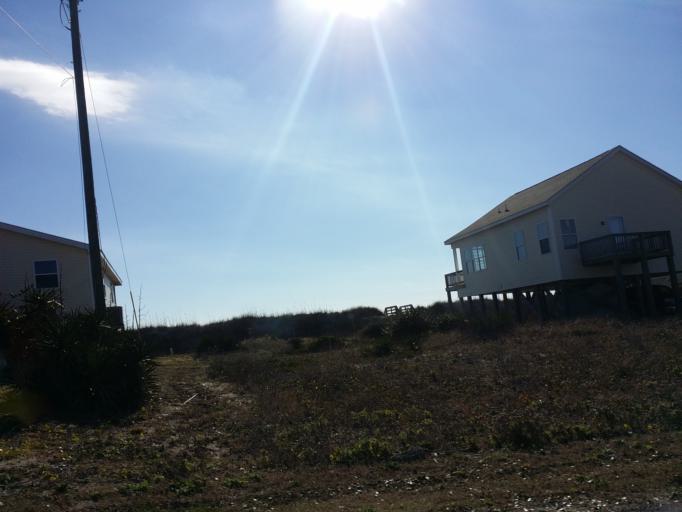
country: US
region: North Carolina
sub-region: Pender County
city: Surf City
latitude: 34.4587
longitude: -77.4897
